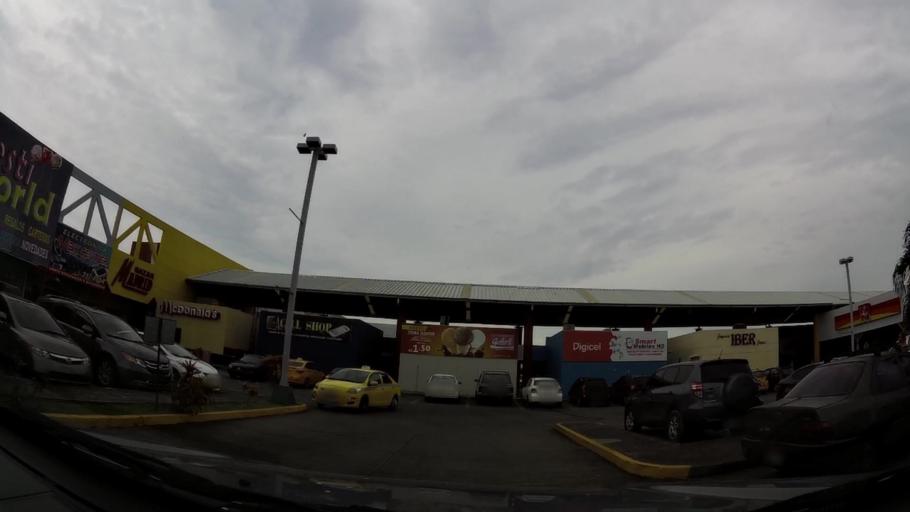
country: PA
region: Panama
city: San Miguelito
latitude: 9.0491
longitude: -79.4496
